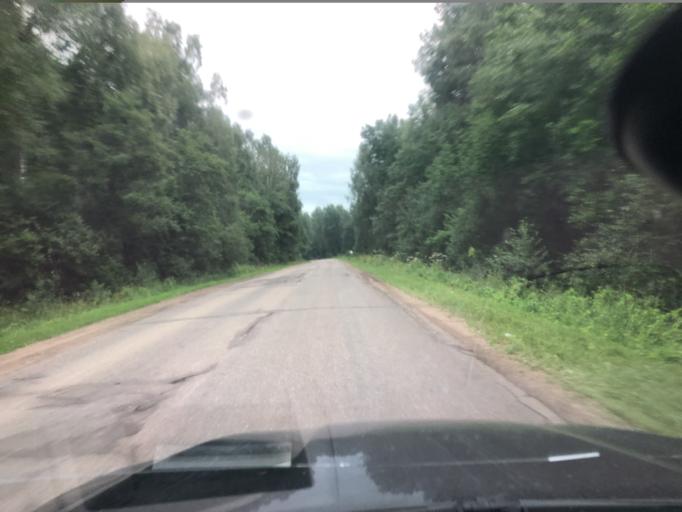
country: RU
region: Jaroslavl
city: Petrovsk
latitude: 56.9859
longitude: 39.2003
